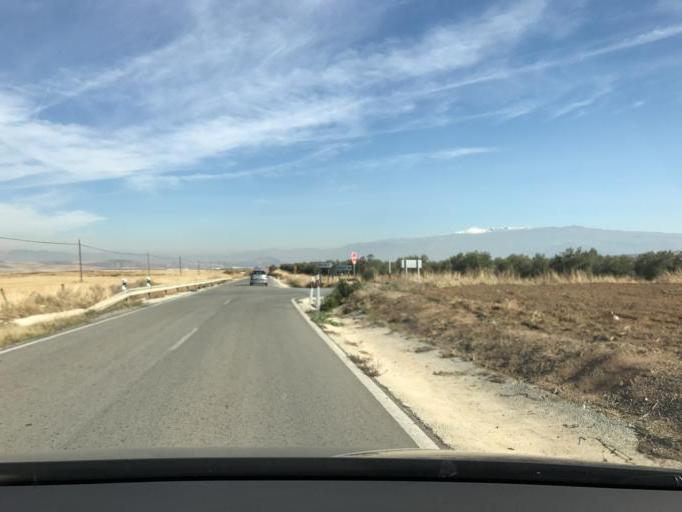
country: ES
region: Andalusia
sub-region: Provincia de Granada
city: Ventas de Huelma
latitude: 37.0737
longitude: -3.8021
